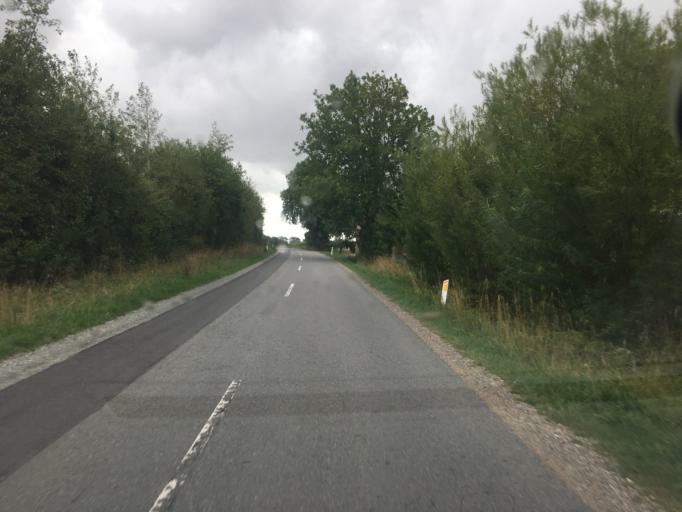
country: DK
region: South Denmark
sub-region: Tonder Kommune
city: Logumkloster
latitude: 54.9986
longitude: 8.9627
